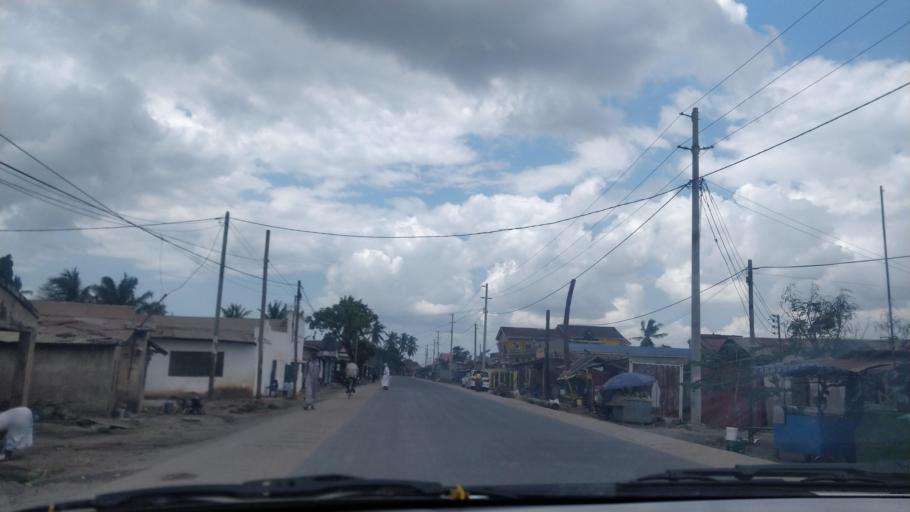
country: TZ
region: Dar es Salaam
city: Magomeni
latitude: -6.8067
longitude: 39.2302
